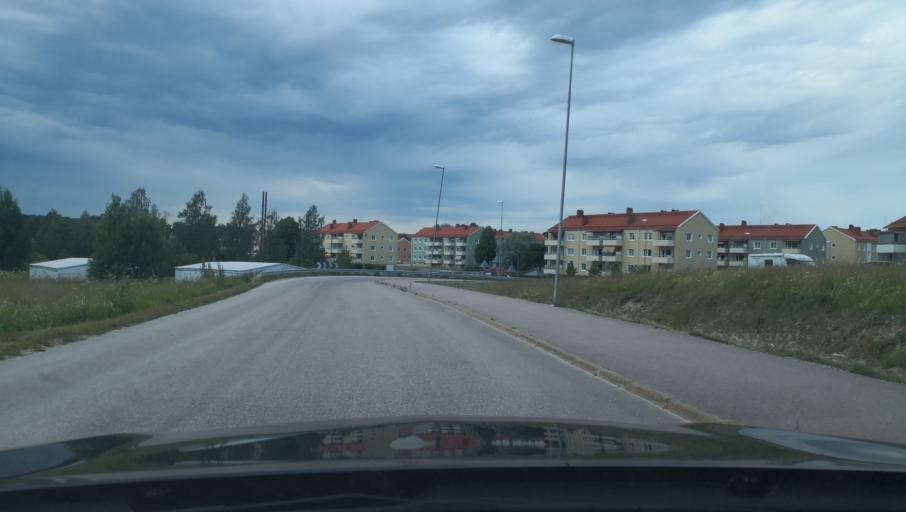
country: SE
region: Vaestmanland
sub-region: Fagersta Kommun
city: Fagersta
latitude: 59.9849
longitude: 15.8250
